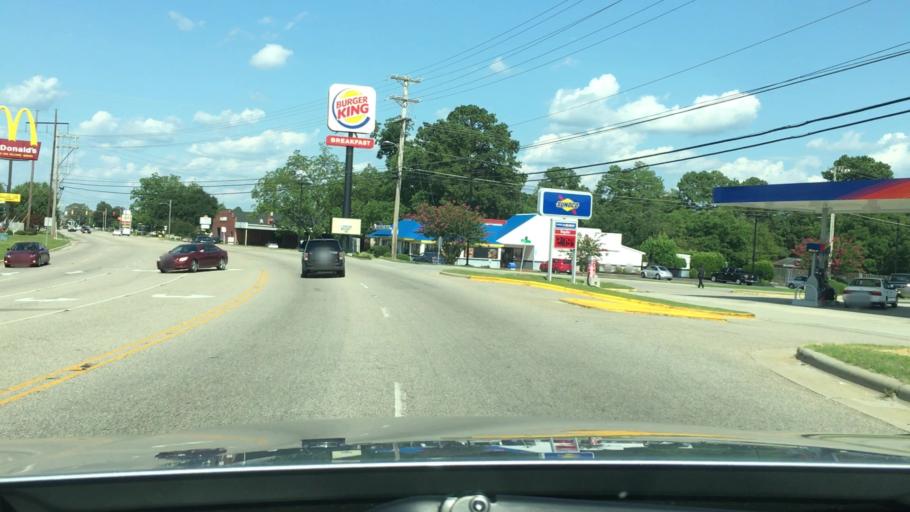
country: US
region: North Carolina
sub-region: Robeson County
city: Lumberton
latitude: 34.6221
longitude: -79.0496
